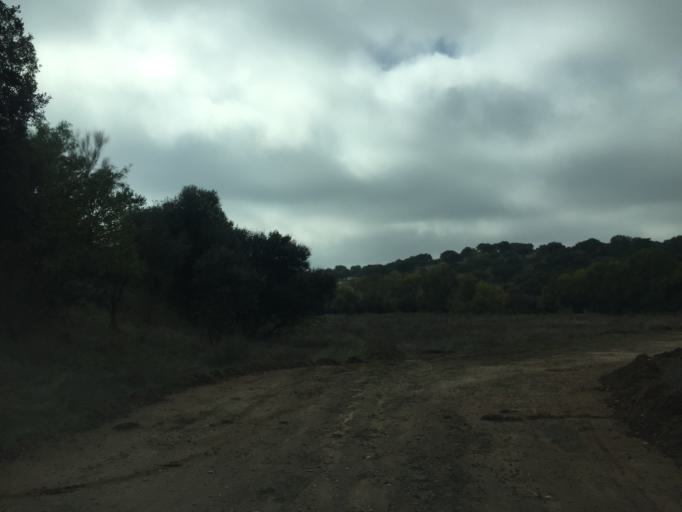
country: PT
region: Portalegre
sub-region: Fronteira
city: Fronteira
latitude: 39.0677
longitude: -7.6174
